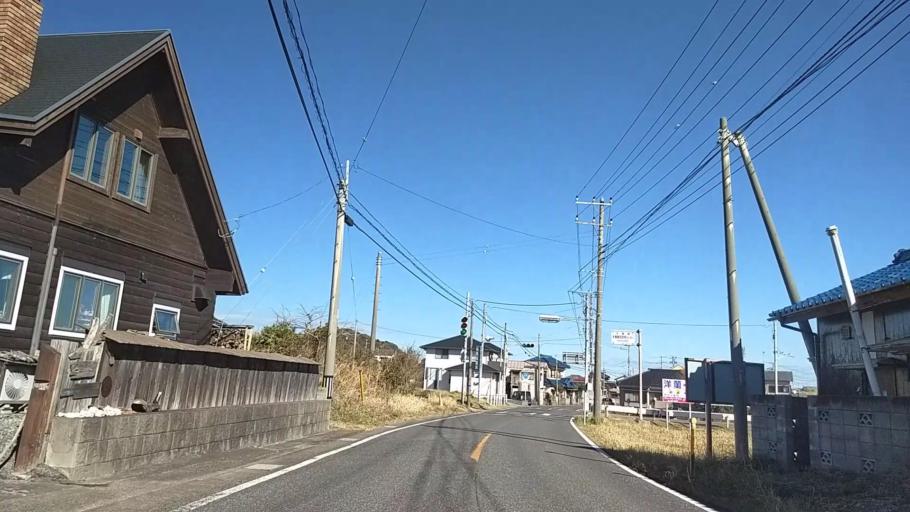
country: JP
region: Chiba
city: Tateyama
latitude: 34.9408
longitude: 139.9567
